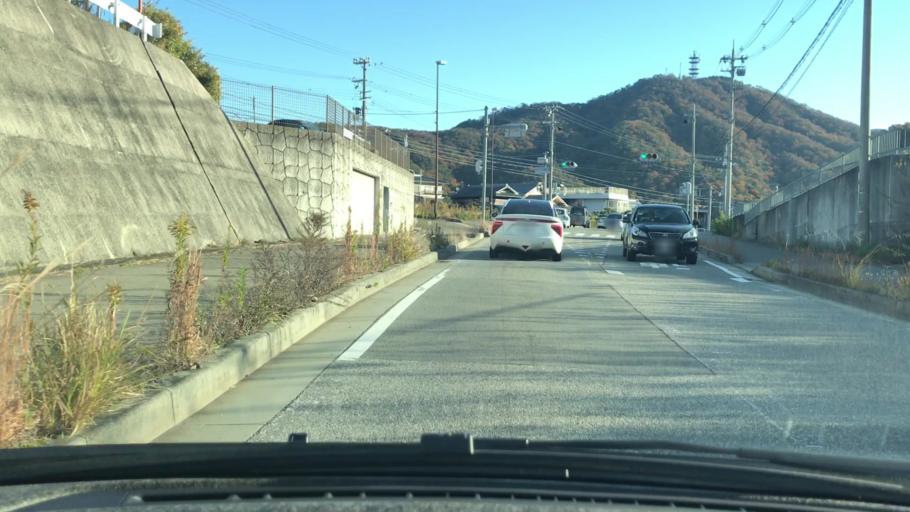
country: JP
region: Hyogo
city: Sandacho
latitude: 34.8219
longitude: 135.2511
